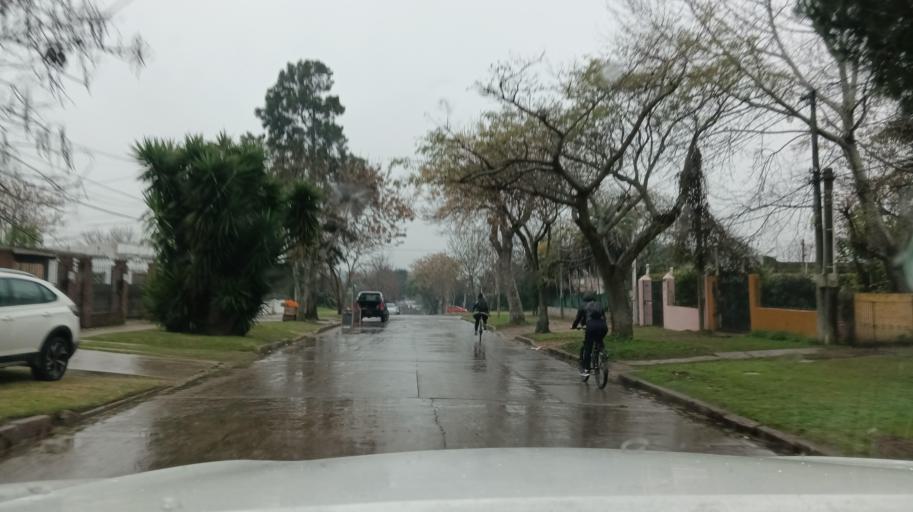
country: UY
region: Canelones
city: Paso de Carrasco
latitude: -34.8754
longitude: -56.0874
